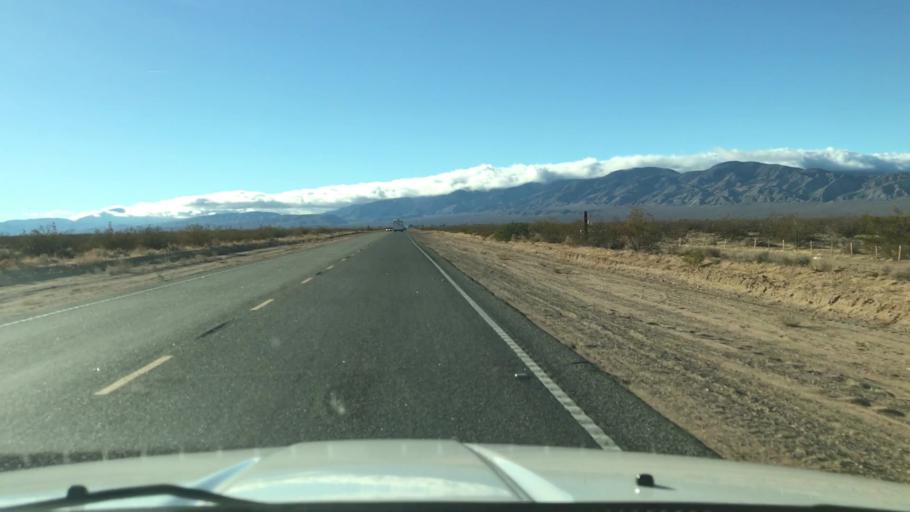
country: US
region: California
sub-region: Kern County
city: California City
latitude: 35.1255
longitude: -118.0530
